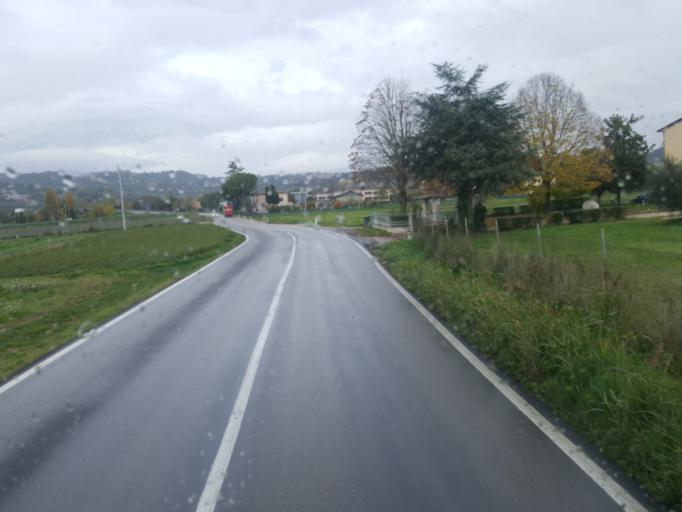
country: IT
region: Umbria
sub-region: Provincia di Perugia
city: San Martino in Campo
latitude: 43.0733
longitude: 12.4252
